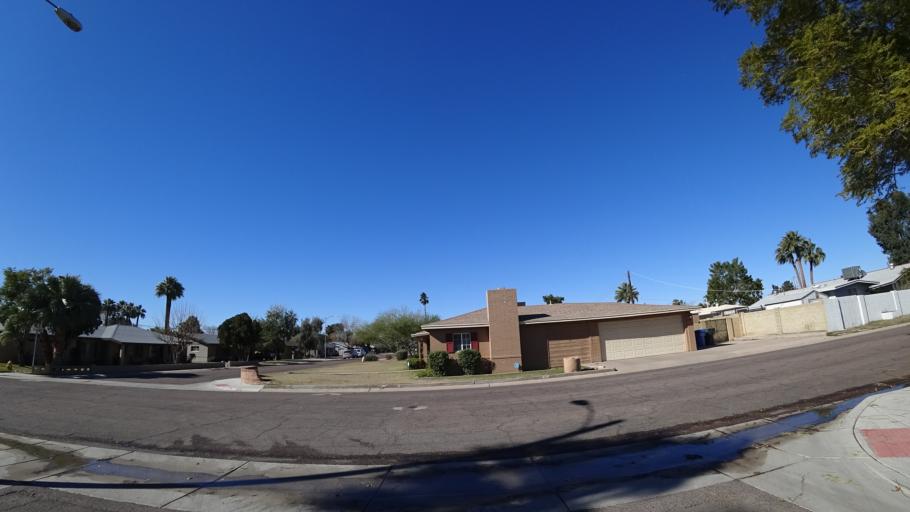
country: US
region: Arizona
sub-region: Maricopa County
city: Phoenix
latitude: 33.5137
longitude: -112.0584
